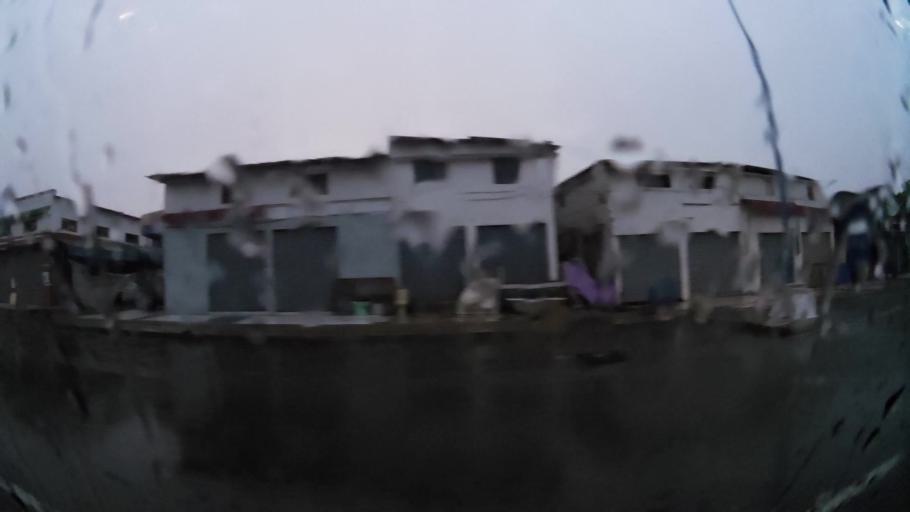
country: MA
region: Grand Casablanca
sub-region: Casablanca
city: Casablanca
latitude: 33.5619
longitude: -7.5993
